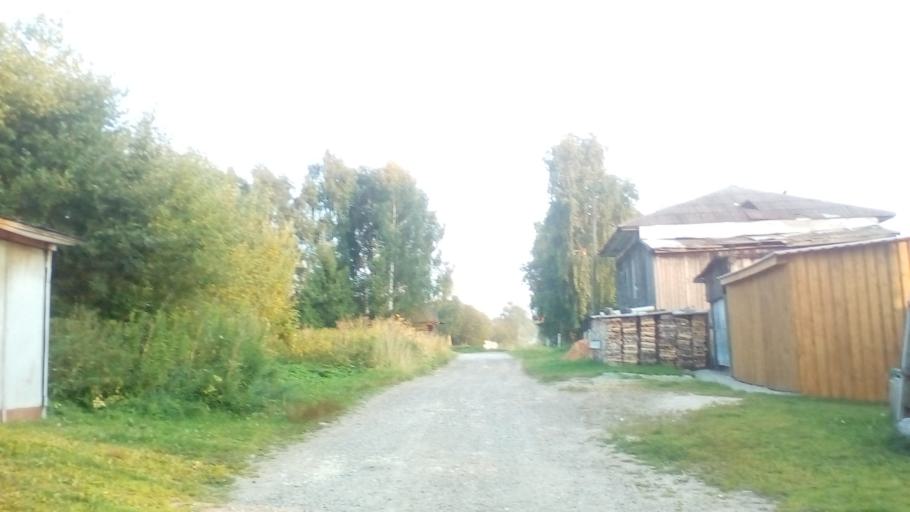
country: RU
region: Perm
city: Usol'ye
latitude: 59.4839
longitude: 56.5874
